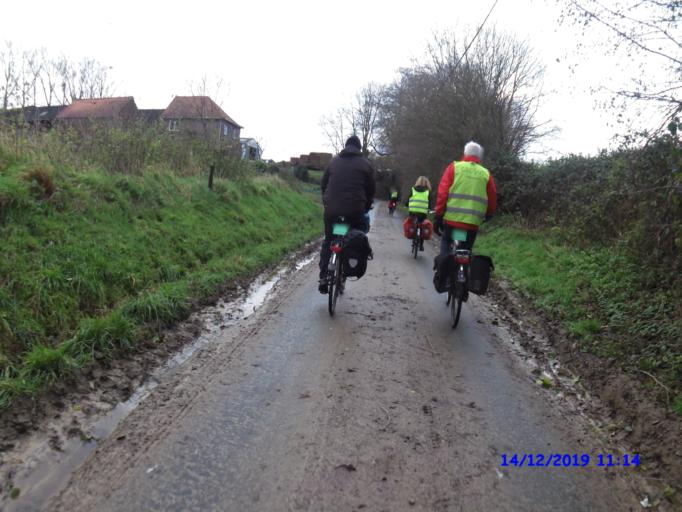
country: BE
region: Flanders
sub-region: Provincie Vlaams-Brabant
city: Beersel
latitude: 50.7454
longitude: 4.3133
